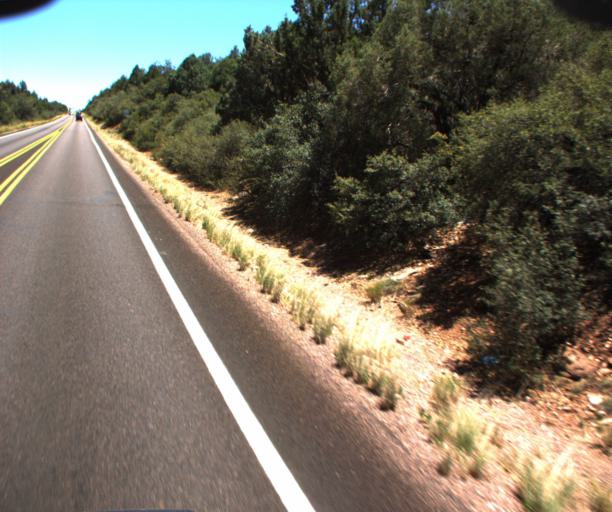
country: US
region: Arizona
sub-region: Gila County
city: Payson
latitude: 34.2935
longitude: -111.3495
